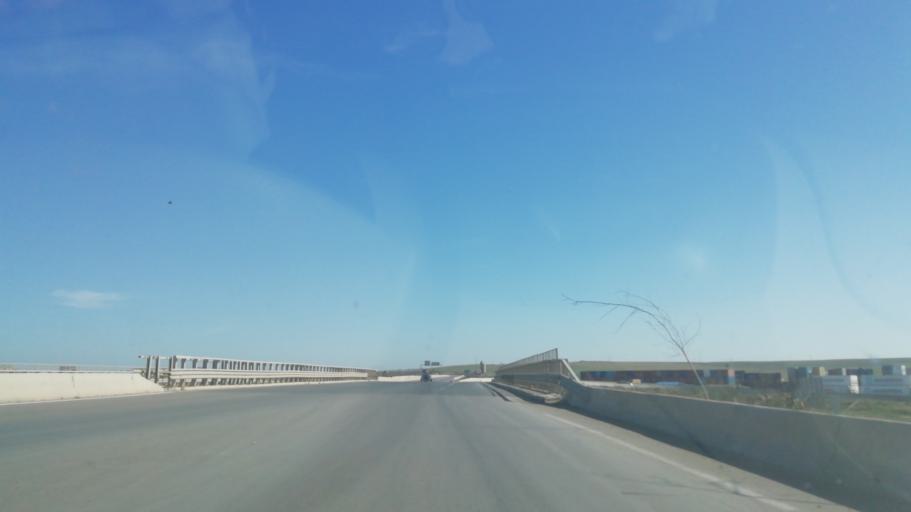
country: DZ
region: Oran
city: Es Senia
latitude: 35.6011
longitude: -0.5750
